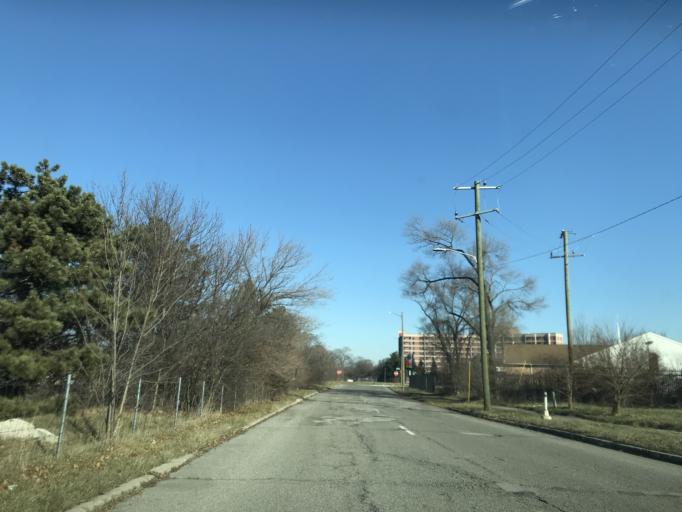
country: US
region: Michigan
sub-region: Wayne County
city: Highland Park
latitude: 42.3436
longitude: -83.1136
